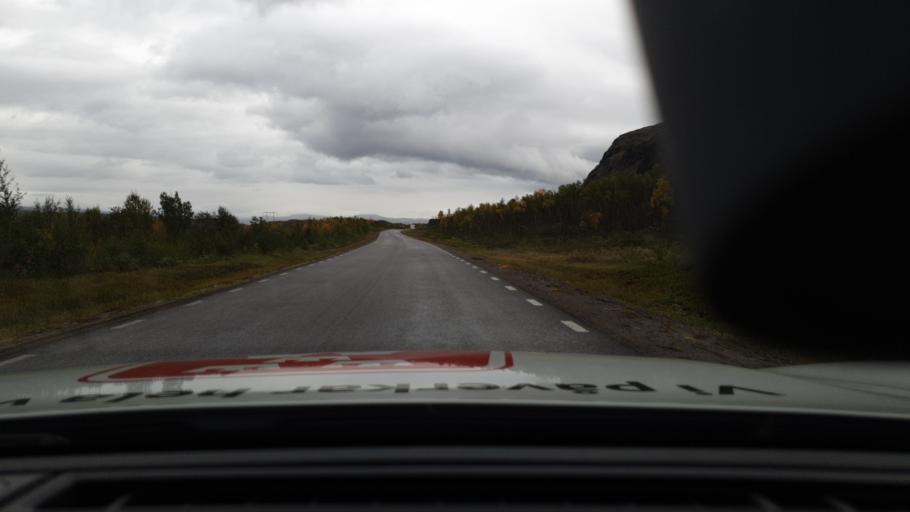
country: NO
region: Troms
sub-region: Bardu
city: Setermoen
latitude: 68.4262
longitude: 18.3613
